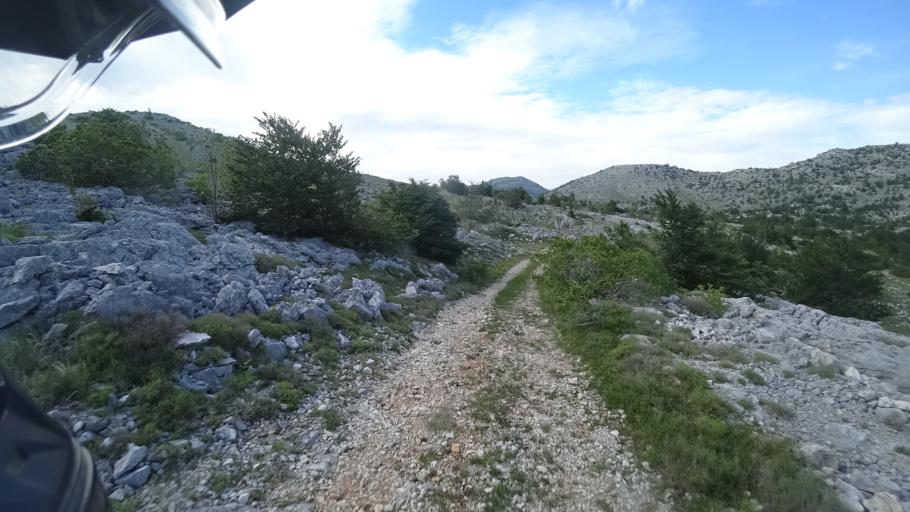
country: HR
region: Splitsko-Dalmatinska
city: Hrvace
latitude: 43.8049
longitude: 16.4332
